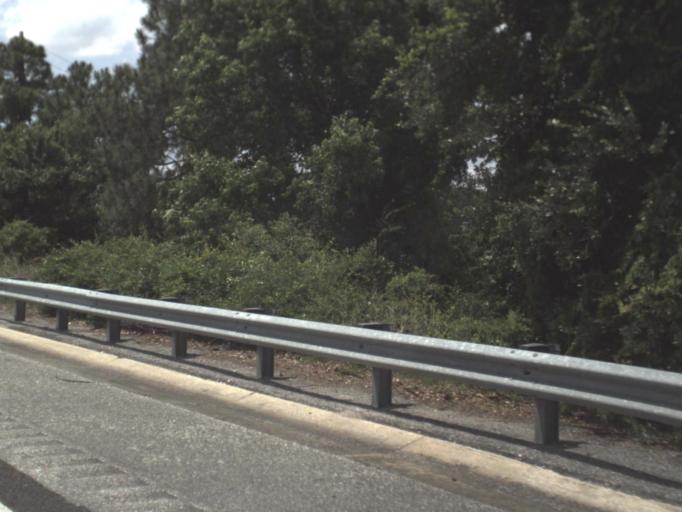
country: US
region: Florida
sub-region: Saint Johns County
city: Fruit Cove
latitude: 30.1692
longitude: -81.6015
